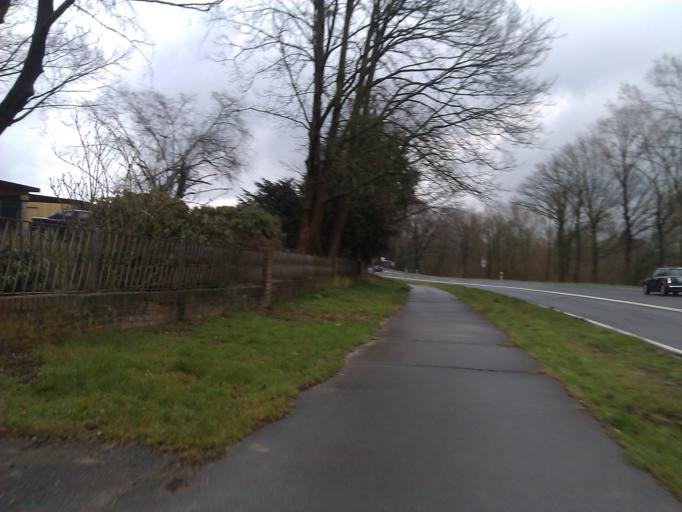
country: DE
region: North Rhine-Westphalia
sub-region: Regierungsbezirk Dusseldorf
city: Heiligenhaus
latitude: 51.3836
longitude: 6.9404
